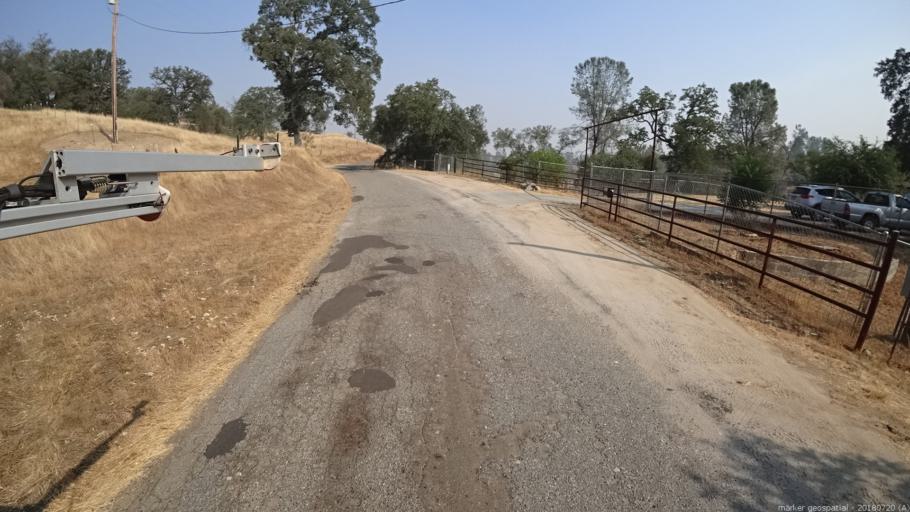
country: US
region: California
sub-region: Madera County
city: Yosemite Lakes
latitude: 37.2950
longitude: -119.8671
